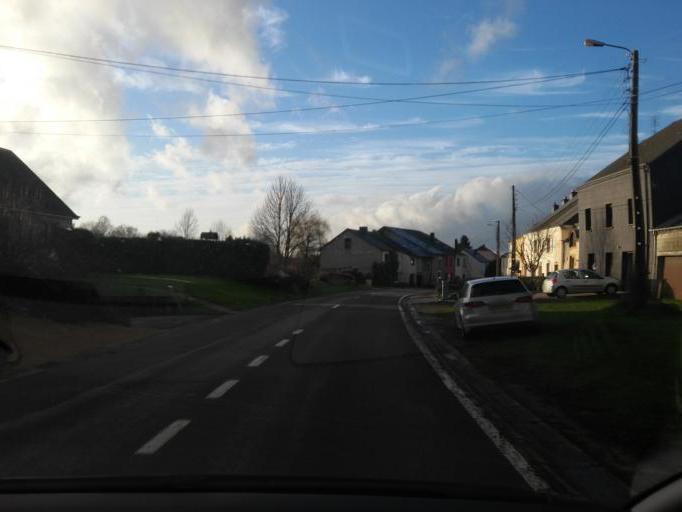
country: BE
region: Wallonia
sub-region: Province du Luxembourg
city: Tintigny
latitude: 49.6632
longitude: 5.4959
